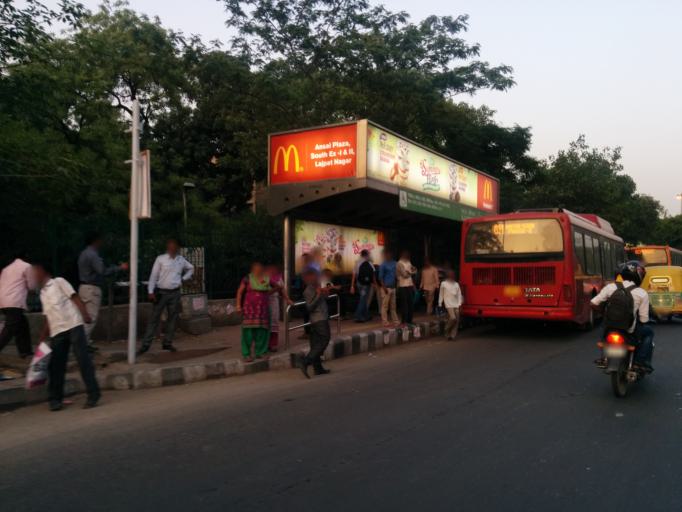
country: IN
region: NCT
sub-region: New Delhi
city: New Delhi
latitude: 28.5698
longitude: 77.2043
